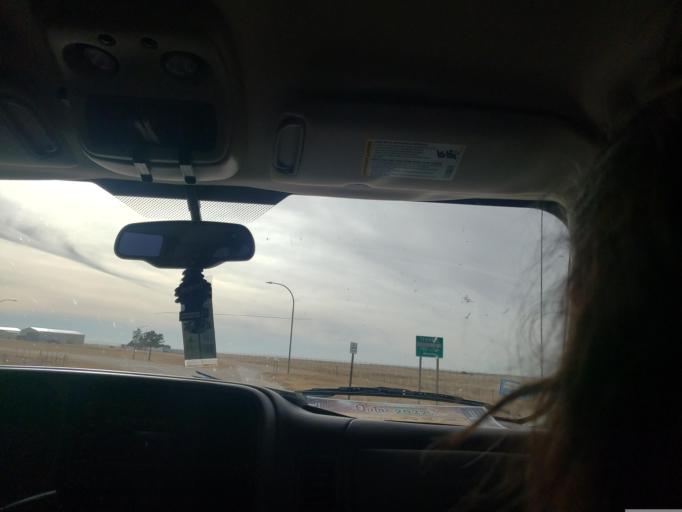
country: US
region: Kansas
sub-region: Finney County
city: Garden City
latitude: 37.9370
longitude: -100.7175
